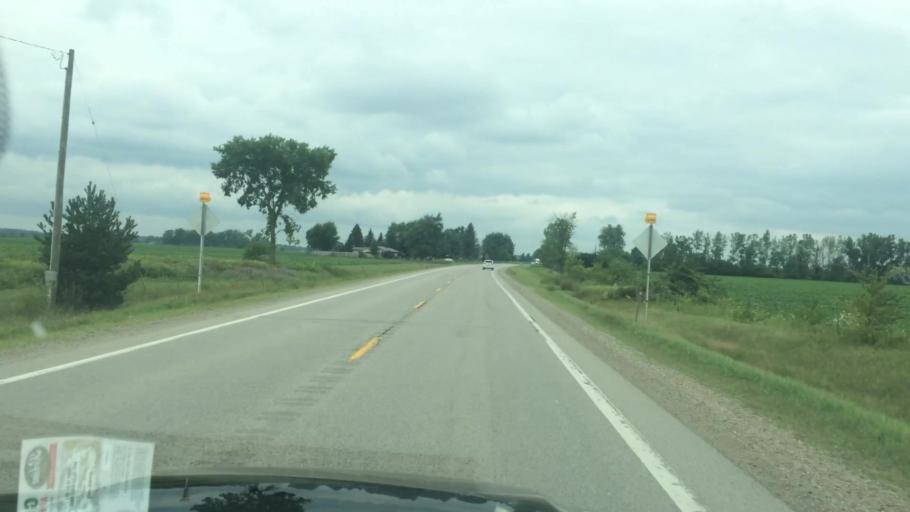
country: US
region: Michigan
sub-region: Sanilac County
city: Marlette
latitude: 43.4186
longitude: -83.0876
